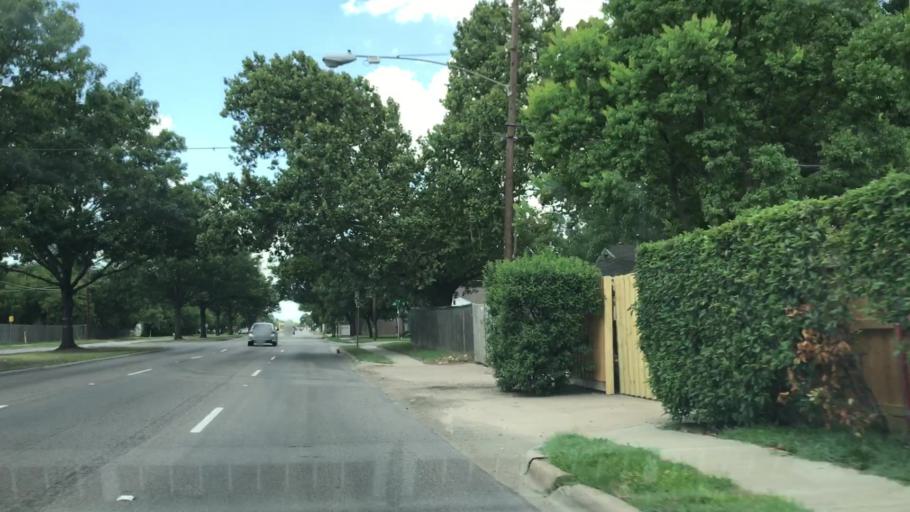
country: US
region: Texas
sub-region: Dallas County
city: University Park
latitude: 32.8725
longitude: -96.8561
